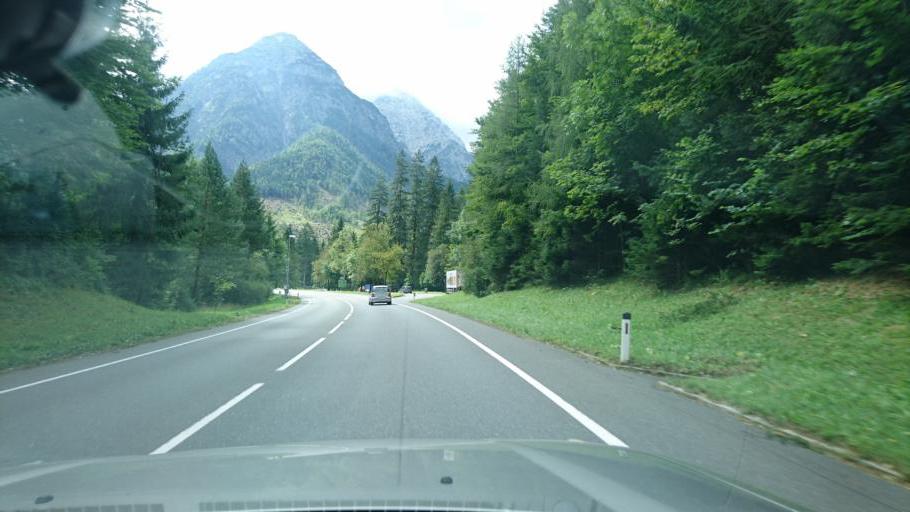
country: AT
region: Salzburg
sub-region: Politischer Bezirk Zell am See
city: Sankt Martin bei Lofer
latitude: 47.5398
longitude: 12.7193
